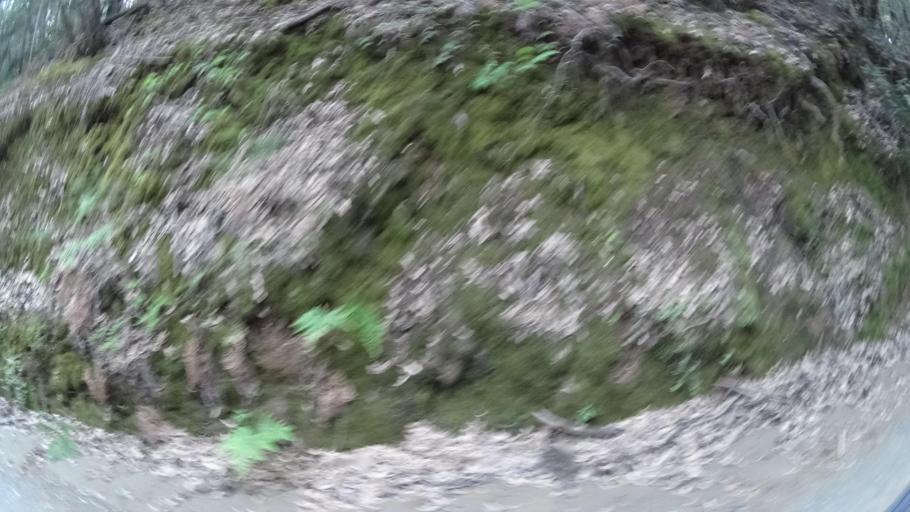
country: US
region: California
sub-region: Humboldt County
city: Redway
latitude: 40.0418
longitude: -123.8482
